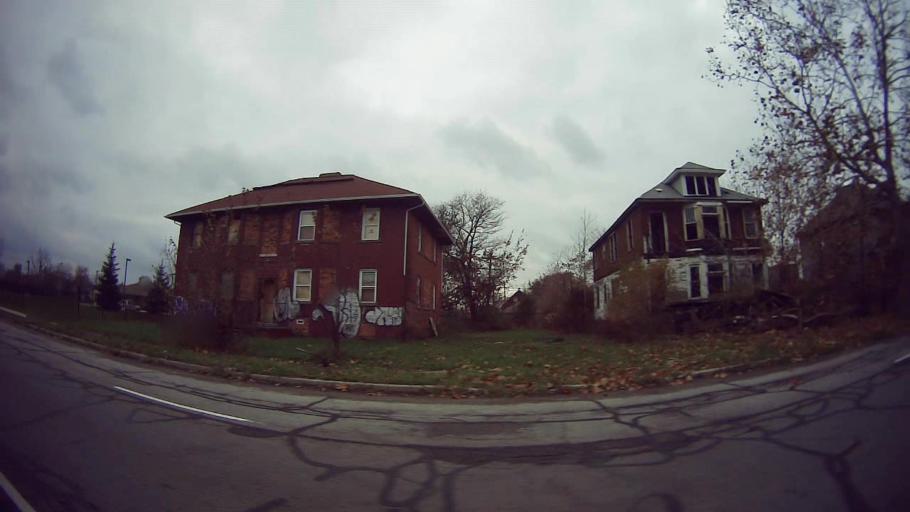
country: US
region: Michigan
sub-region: Wayne County
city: Highland Park
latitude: 42.3617
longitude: -83.0896
